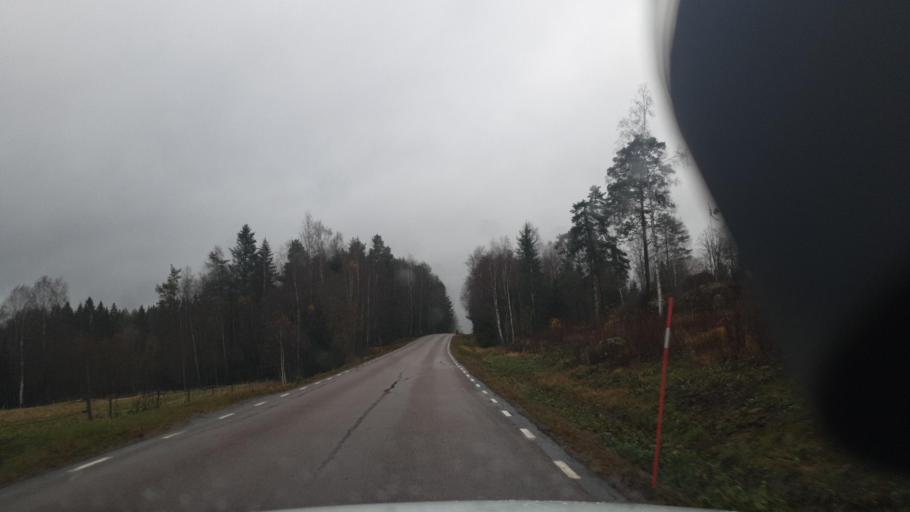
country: SE
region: Vaermland
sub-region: Eda Kommun
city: Charlottenberg
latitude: 59.7678
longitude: 12.2079
